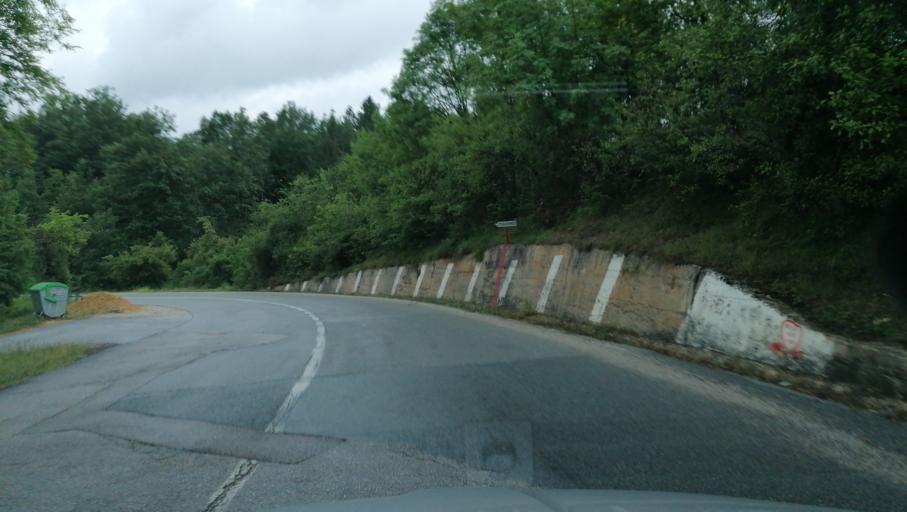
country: RS
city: Durici
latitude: 43.8092
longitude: 19.5096
